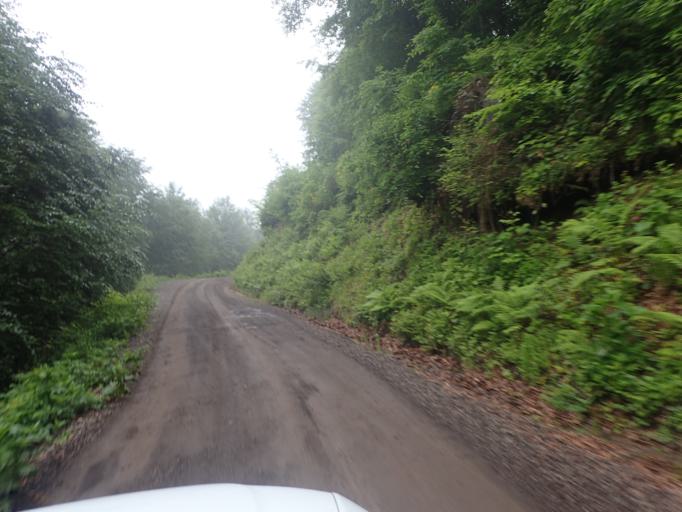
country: TR
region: Samsun
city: Salipazari
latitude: 40.9357
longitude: 36.8784
